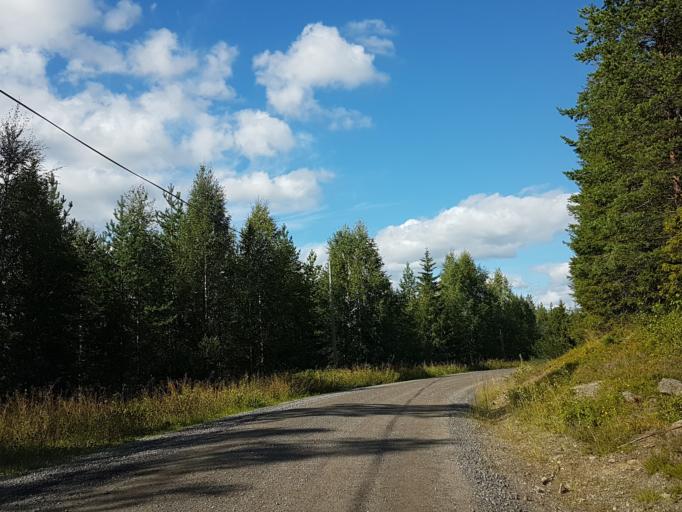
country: SE
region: Vaesterbotten
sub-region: Skelleftea Kommun
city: Burtraesk
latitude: 64.2759
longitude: 20.4795
